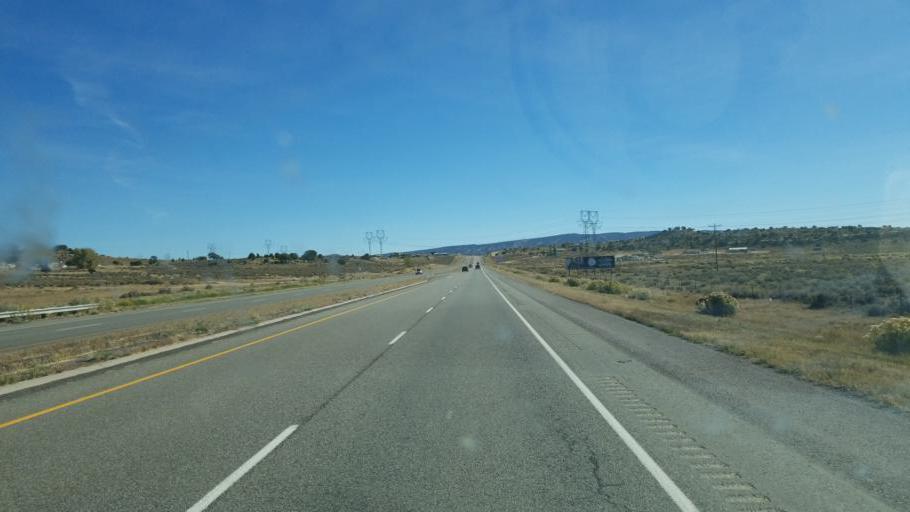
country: US
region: New Mexico
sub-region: McKinley County
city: Twin Lakes
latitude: 35.6327
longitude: -108.8071
